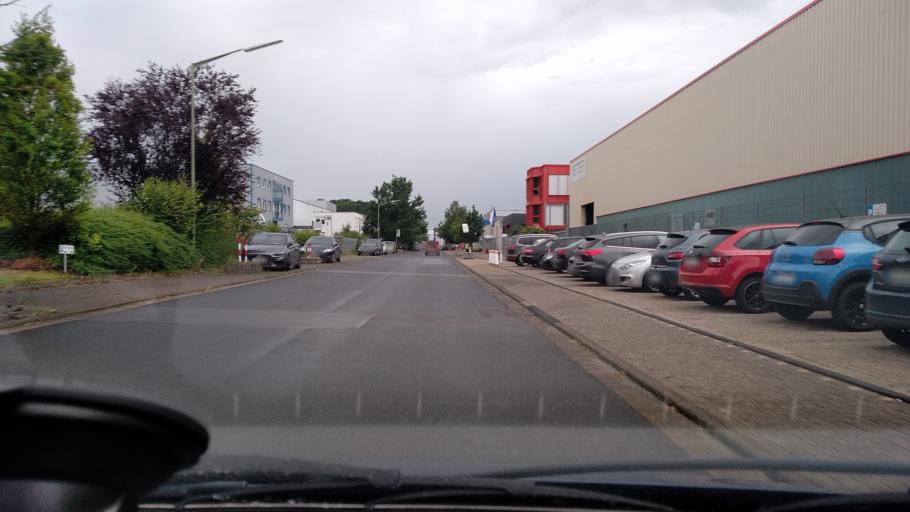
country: DE
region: North Rhine-Westphalia
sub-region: Regierungsbezirk Arnsberg
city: Burbach
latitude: 50.7554
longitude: 8.1204
